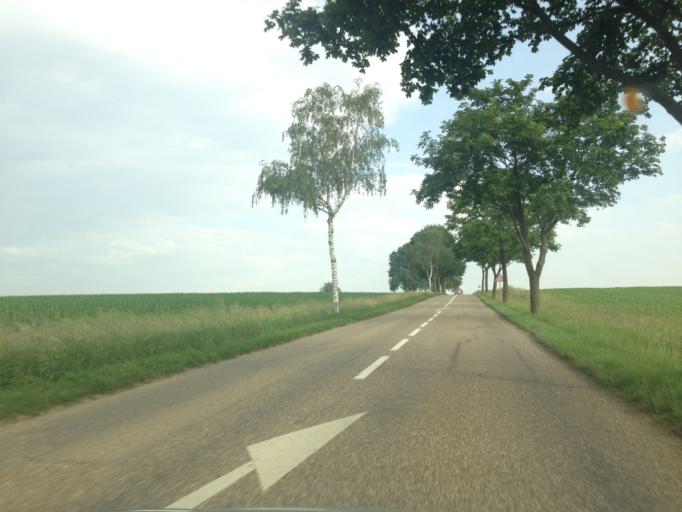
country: FR
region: Alsace
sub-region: Departement du Bas-Rhin
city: Schwindratzheim
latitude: 48.7748
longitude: 7.5927
